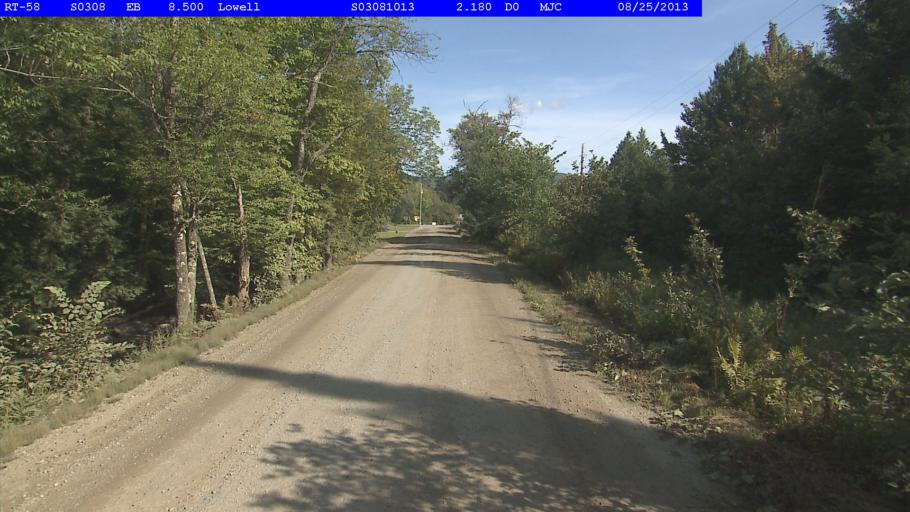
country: US
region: Vermont
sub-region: Lamoille County
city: Hyde Park
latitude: 44.8174
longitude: -72.4735
